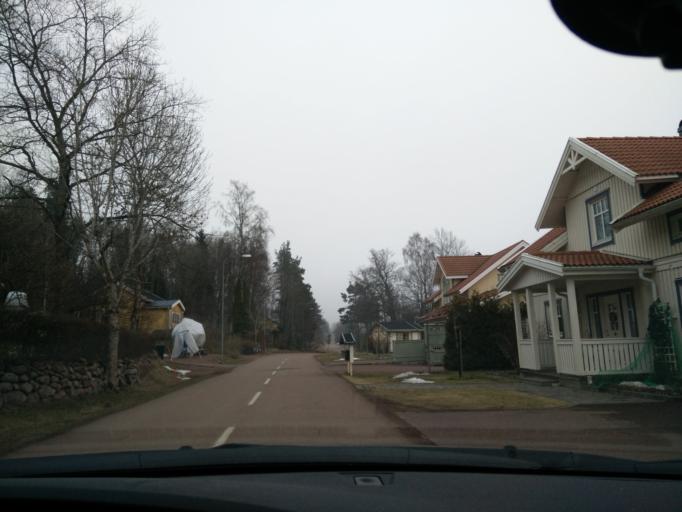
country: AX
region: Mariehamns stad
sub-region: Mariehamn
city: Mariehamn
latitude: 60.1226
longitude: 19.9245
